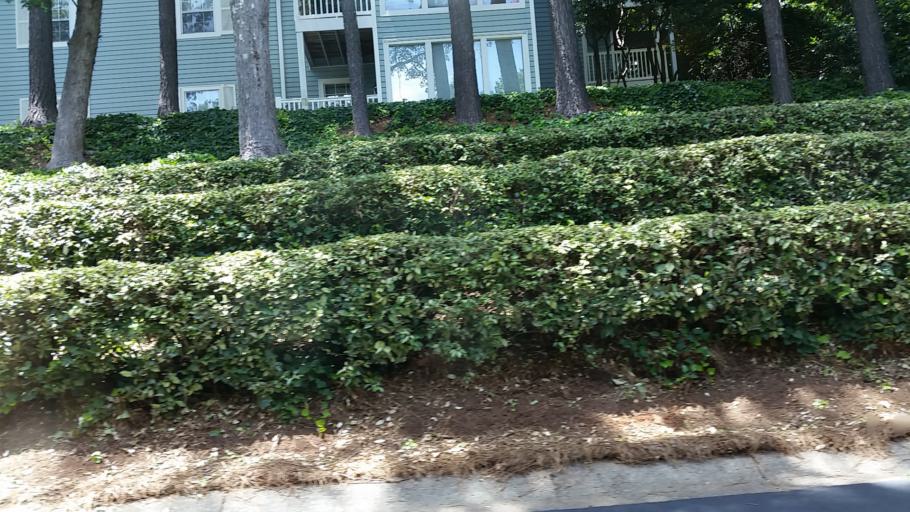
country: US
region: Georgia
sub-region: Cobb County
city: Smyrna
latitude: 33.9161
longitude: -84.4778
